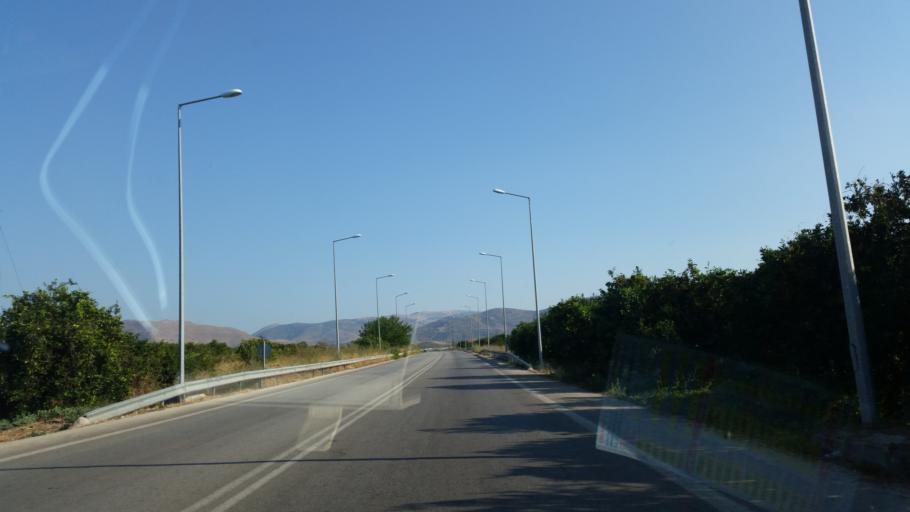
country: GR
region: Peloponnese
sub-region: Nomos Argolidos
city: Nea Tirins
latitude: 37.6227
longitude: 22.8157
